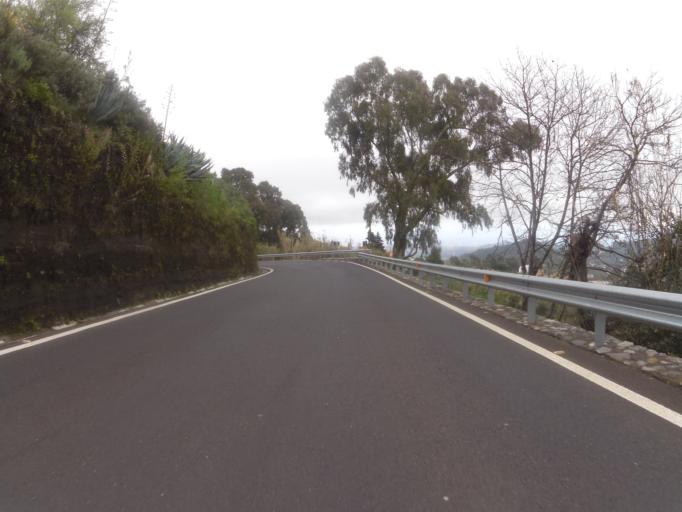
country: ES
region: Canary Islands
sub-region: Provincia de Las Palmas
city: Vega de San Mateo
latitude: 28.0059
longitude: -15.5574
